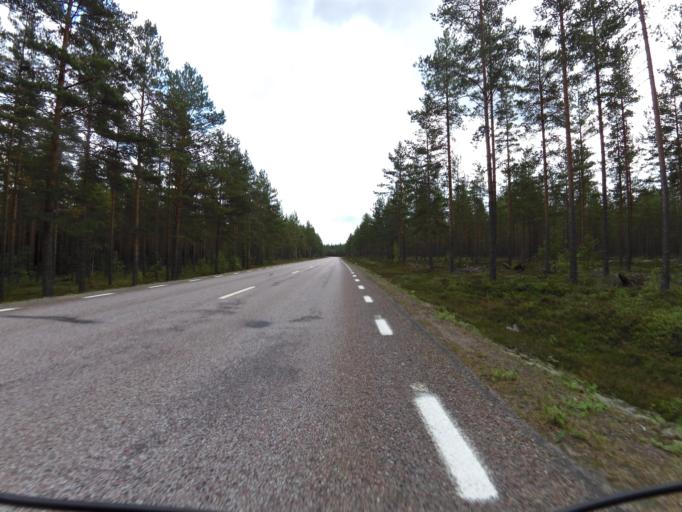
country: SE
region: Gaevleborg
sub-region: Sandvikens Kommun
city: Sandviken
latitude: 60.7261
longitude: 16.7857
